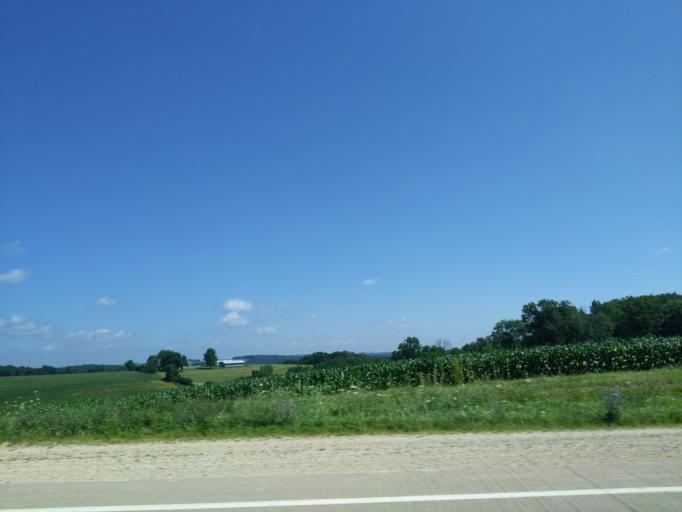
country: US
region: Wisconsin
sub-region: La Crosse County
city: La Crosse
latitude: 43.7311
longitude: -91.0929
